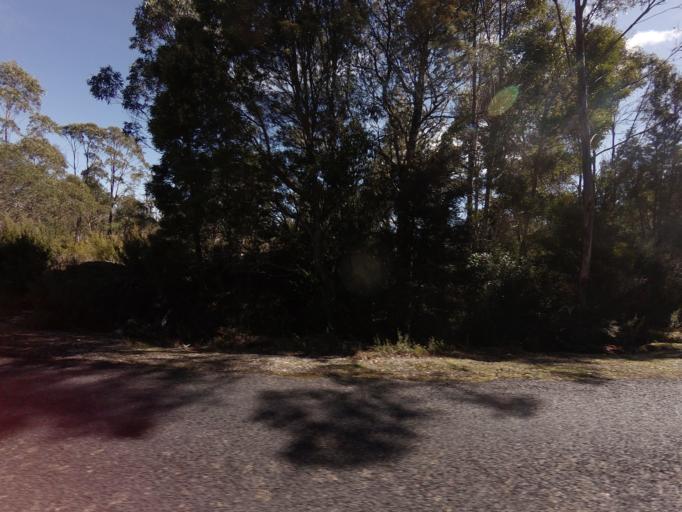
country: AU
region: Tasmania
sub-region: Derwent Valley
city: New Norfolk
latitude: -42.7208
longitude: 146.4409
